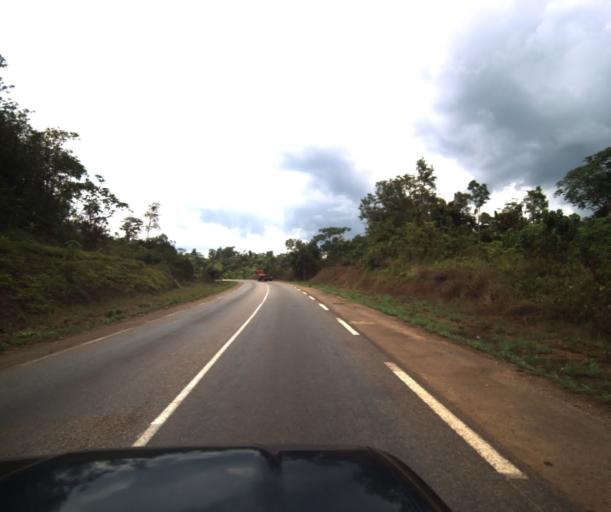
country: CM
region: Littoral
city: Edea
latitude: 3.8798
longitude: 10.0702
